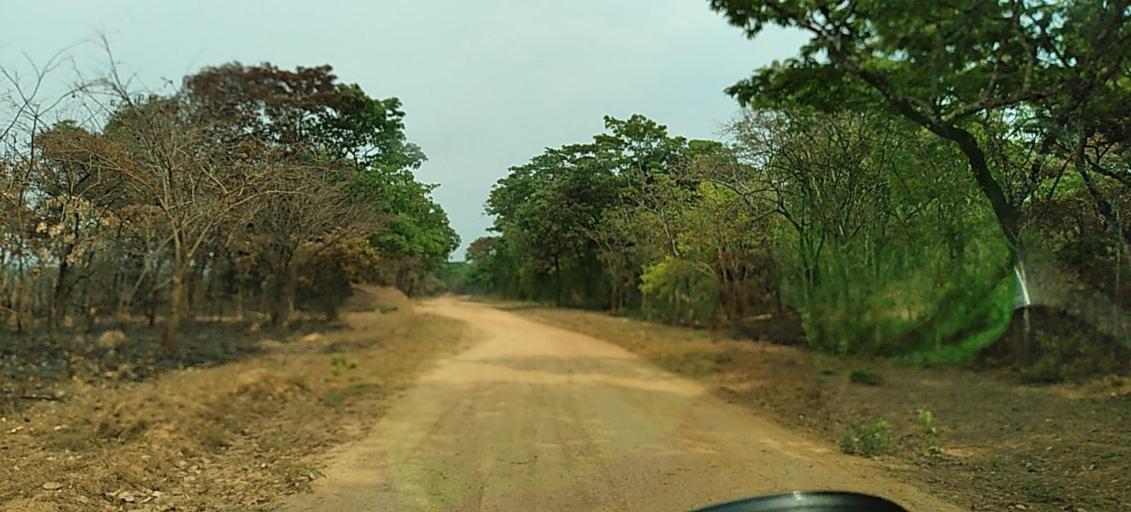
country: ZM
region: North-Western
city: Solwezi
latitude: -12.9570
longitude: 26.5657
